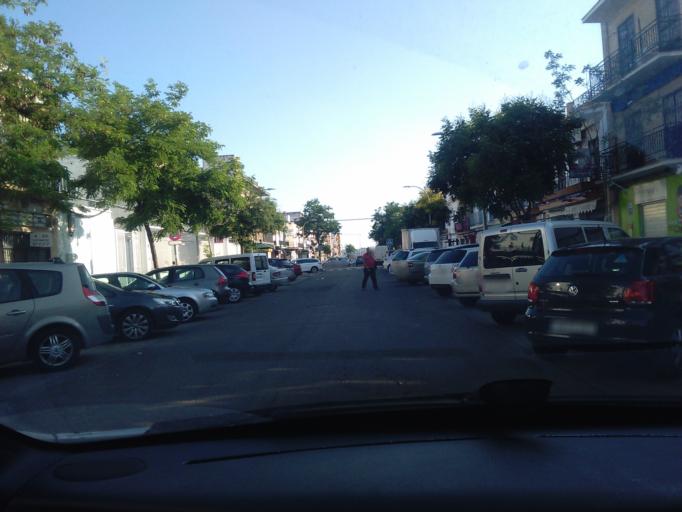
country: ES
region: Andalusia
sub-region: Provincia de Sevilla
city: Sevilla
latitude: 37.3846
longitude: -5.9031
